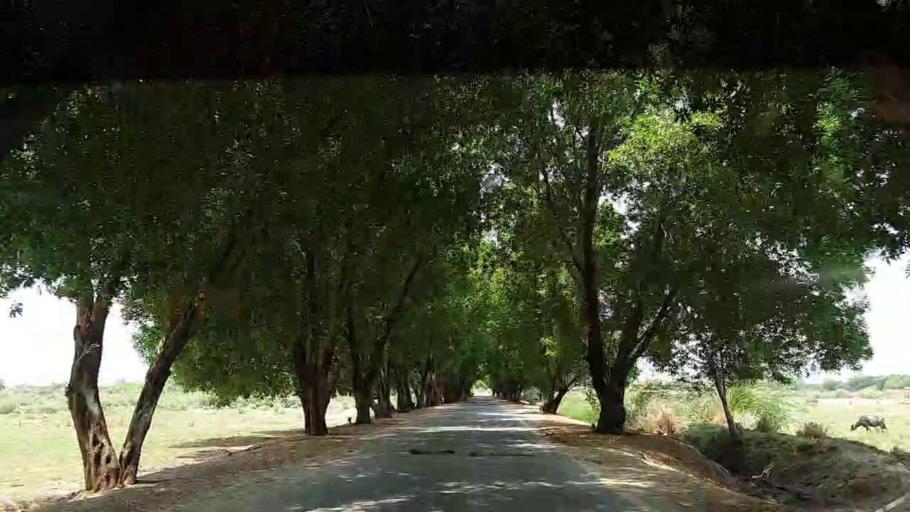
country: PK
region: Sindh
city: Adilpur
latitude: 27.8764
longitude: 69.2726
